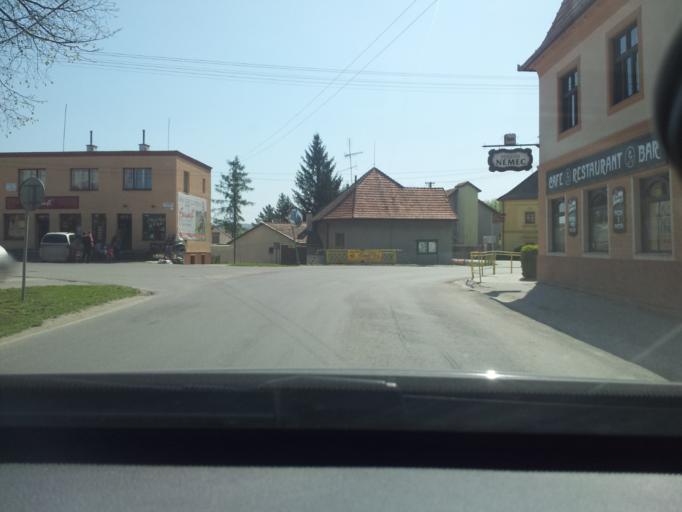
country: SK
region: Nitriansky
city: Partizanske
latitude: 48.6102
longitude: 18.2738
